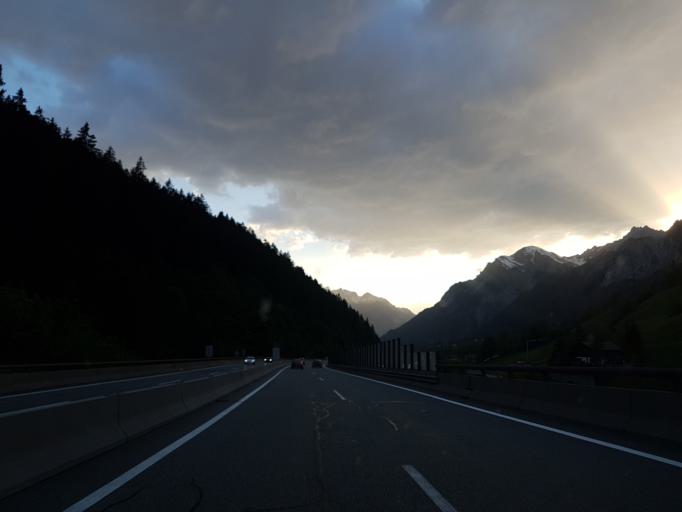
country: AT
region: Vorarlberg
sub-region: Politischer Bezirk Bludenz
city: Klosterle
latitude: 47.1305
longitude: 10.0784
